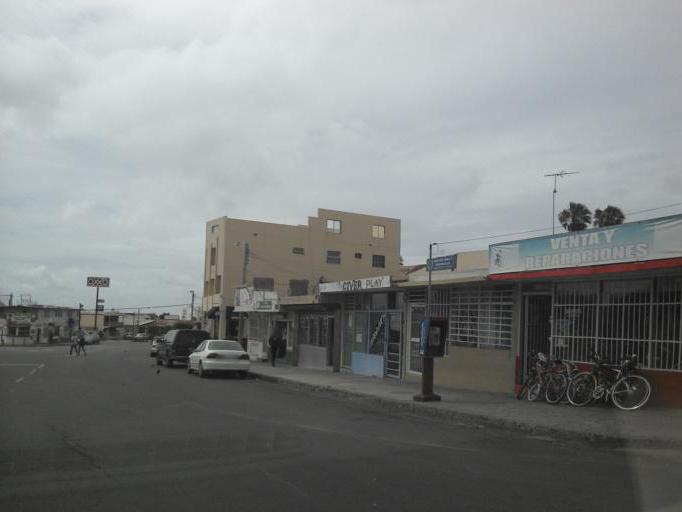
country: MX
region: Baja California
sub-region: Tijuana
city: La Esperanza [Granjas Familiares]
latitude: 32.5093
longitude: -117.1166
